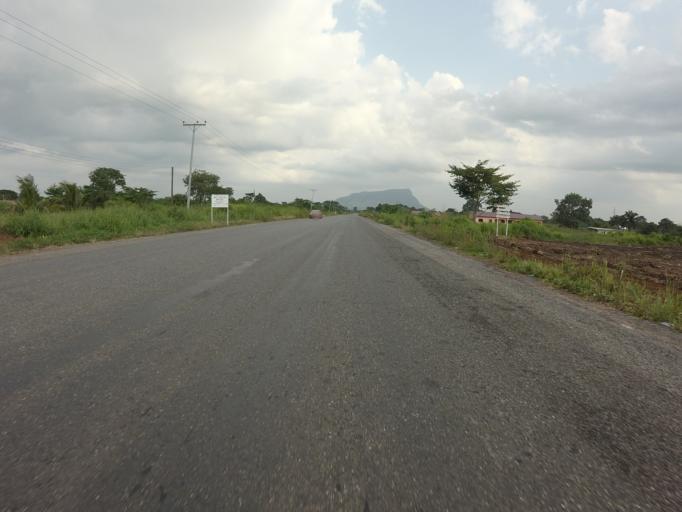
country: GH
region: Volta
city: Ho
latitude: 6.5695
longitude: 0.4856
